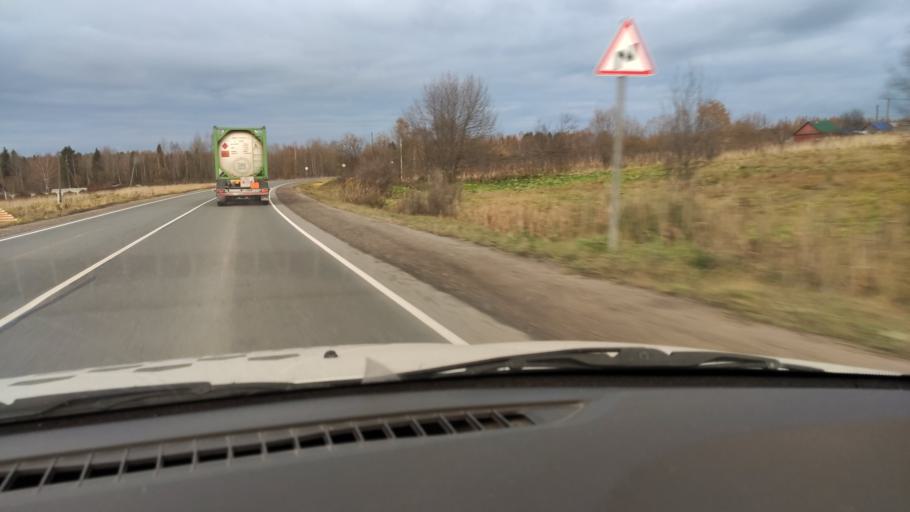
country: RU
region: Kirov
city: Belorechensk
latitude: 58.7154
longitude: 52.3296
